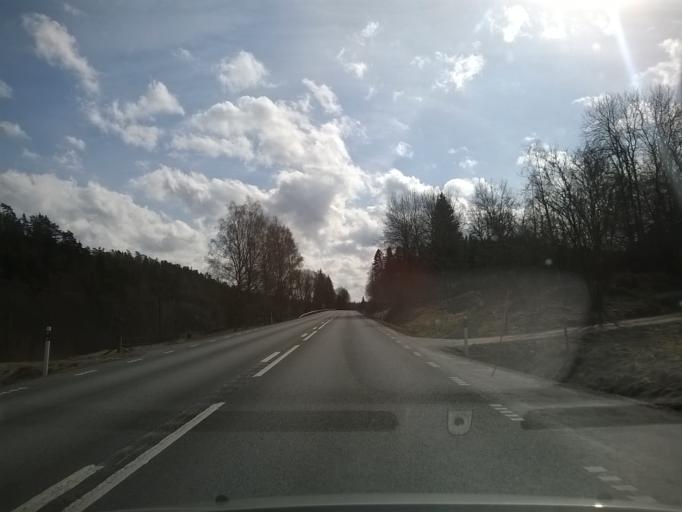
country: SE
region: Vaestra Goetaland
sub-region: Orust
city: Henan
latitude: 58.2173
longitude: 11.6900
